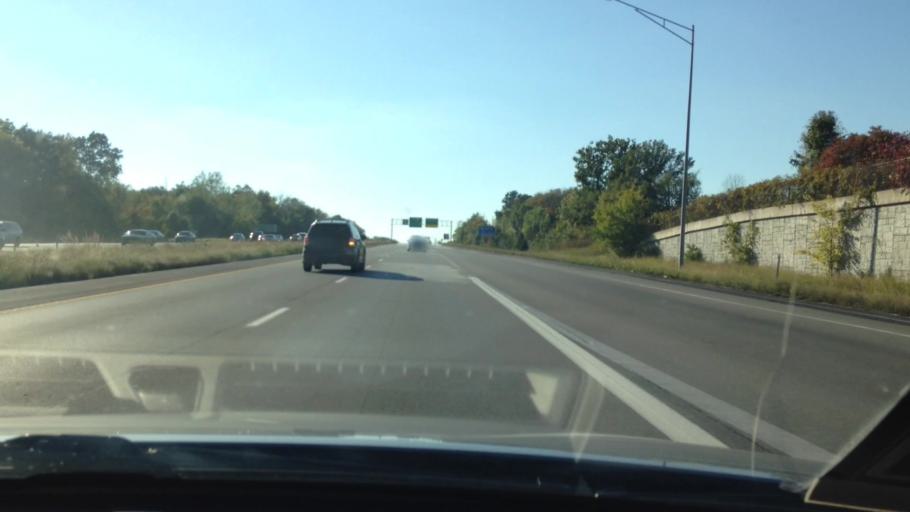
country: US
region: Missouri
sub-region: Platte County
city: Weatherby Lake
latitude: 39.2544
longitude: -94.6364
